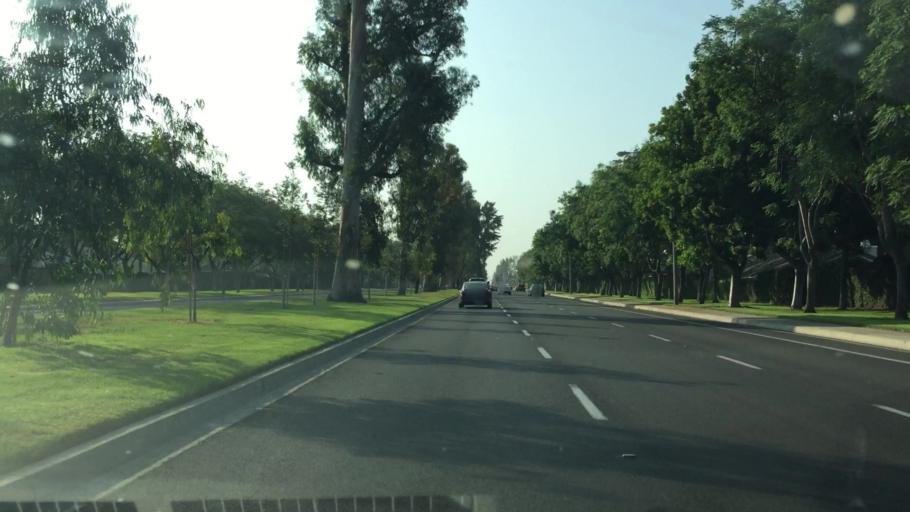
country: US
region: California
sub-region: Orange County
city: North Tustin
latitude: 33.7166
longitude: -117.7641
